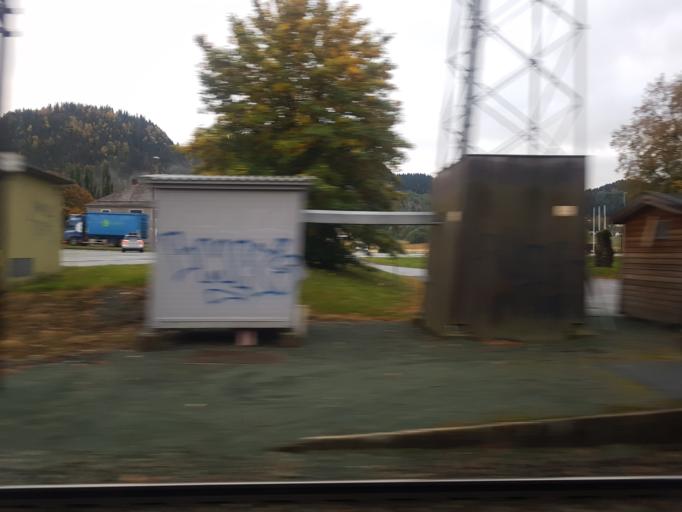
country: NO
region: Sor-Trondelag
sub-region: Melhus
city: Lundamo
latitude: 63.1367
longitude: 10.2618
